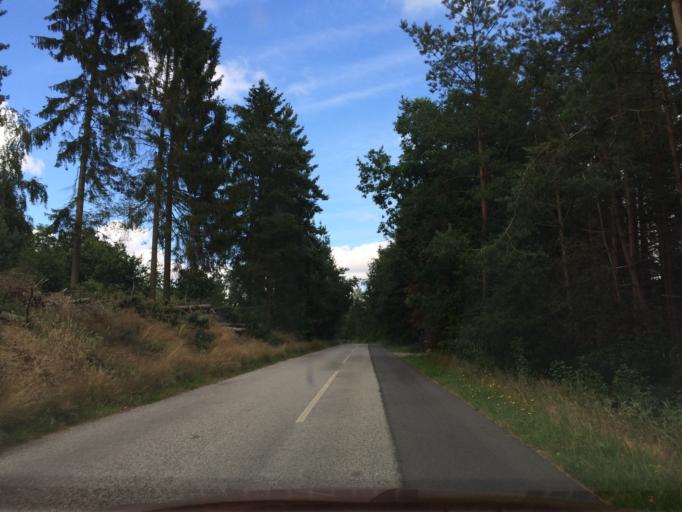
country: DK
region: Central Jutland
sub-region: Silkeborg Kommune
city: Svejbaek
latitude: 56.2077
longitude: 9.6545
